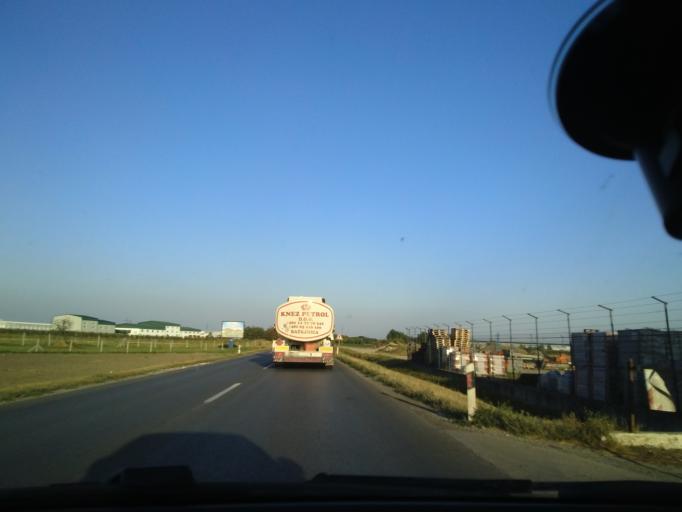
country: RS
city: Rumenka
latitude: 45.2867
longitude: 19.7590
